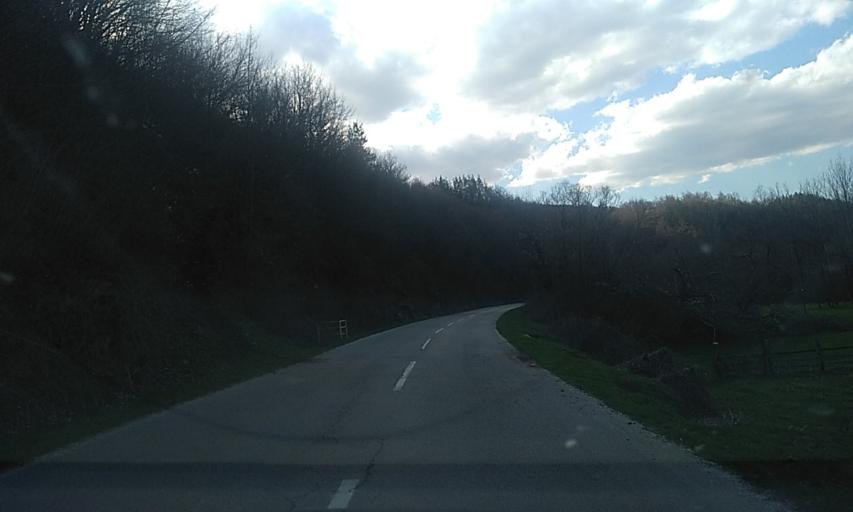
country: RS
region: Central Serbia
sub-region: Pcinjski Okrug
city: Bosilegrad
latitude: 42.4375
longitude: 22.5077
